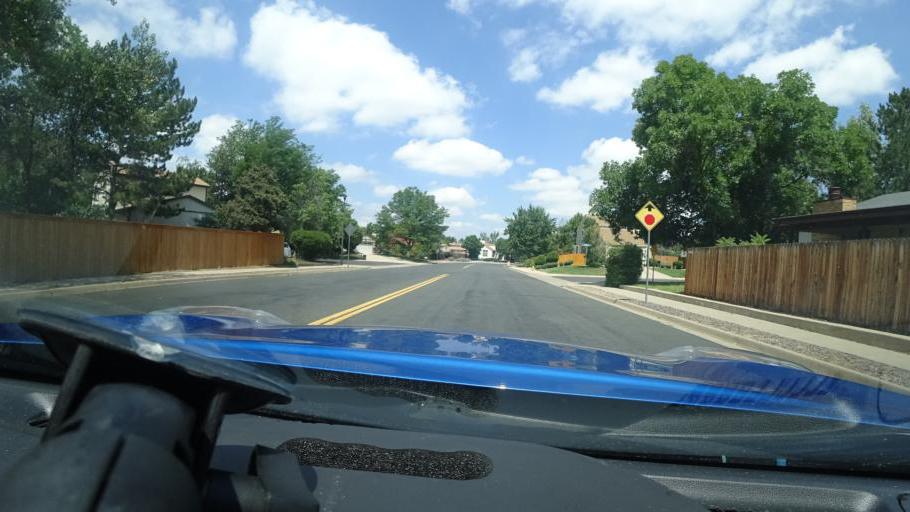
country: US
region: Colorado
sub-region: Adams County
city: Aurora
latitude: 39.7151
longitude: -104.8558
